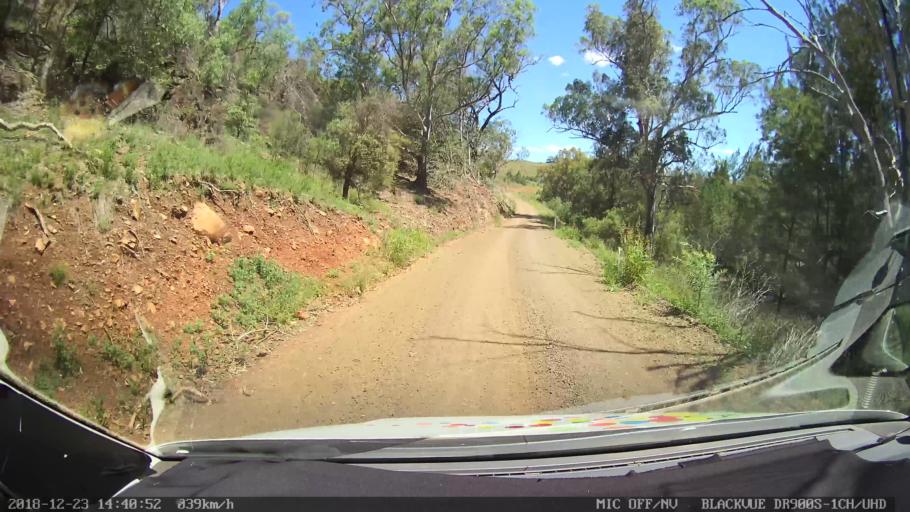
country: AU
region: New South Wales
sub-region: Tamworth Municipality
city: Manilla
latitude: -30.6284
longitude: 150.9029
